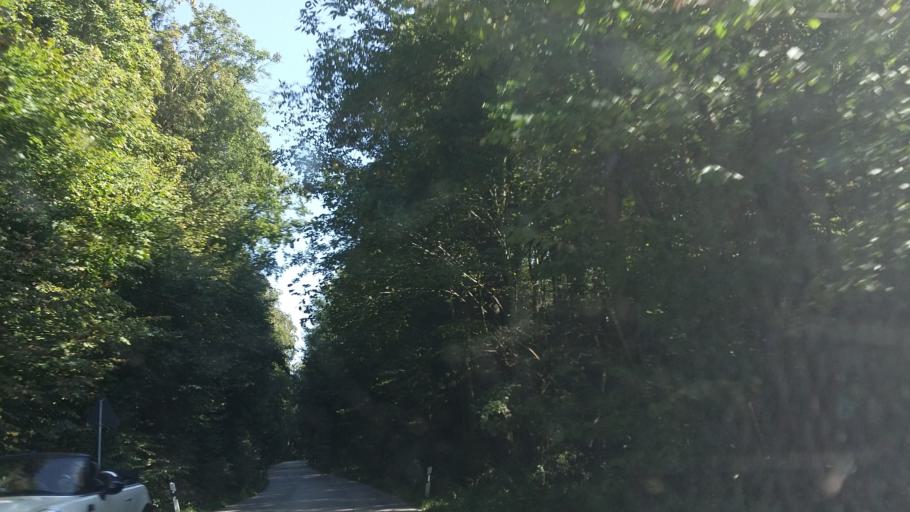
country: DE
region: Bavaria
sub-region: Upper Bavaria
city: Gilching
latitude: 48.0915
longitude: 11.3304
